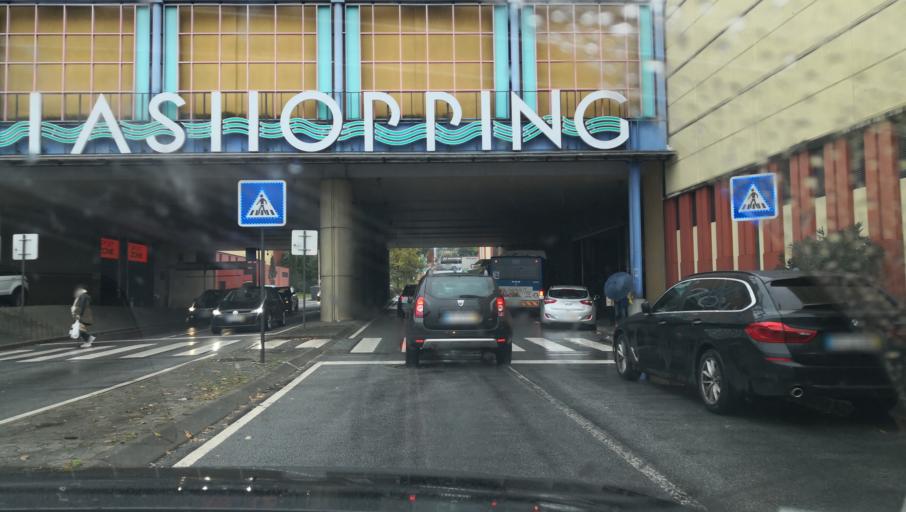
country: PT
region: Porto
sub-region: Vila Nova de Gaia
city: Vila Nova de Gaia
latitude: 41.1188
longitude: -8.6224
